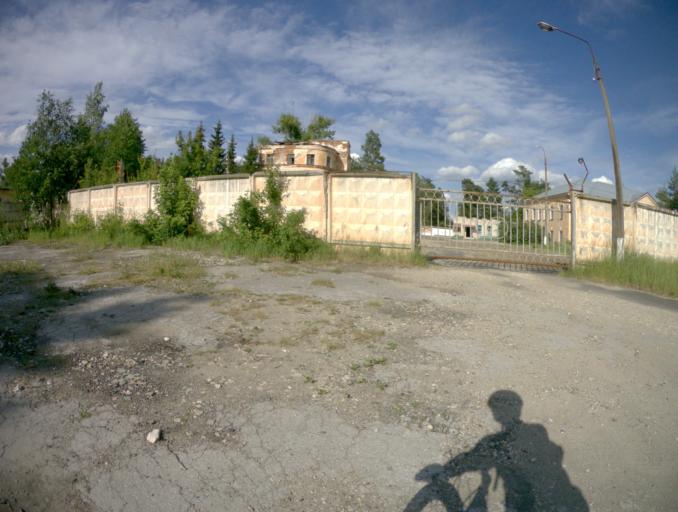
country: RU
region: Vladimir
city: Gorokhovets
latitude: 56.2956
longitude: 42.7852
